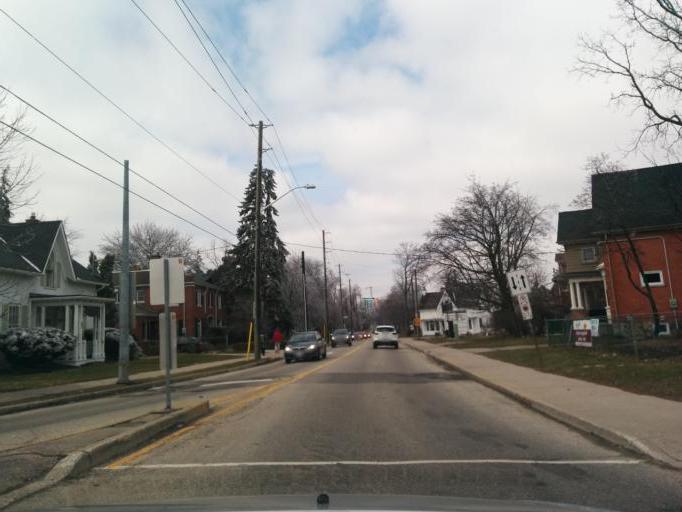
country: CA
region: Ontario
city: Waterloo
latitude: 43.4673
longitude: -80.5251
